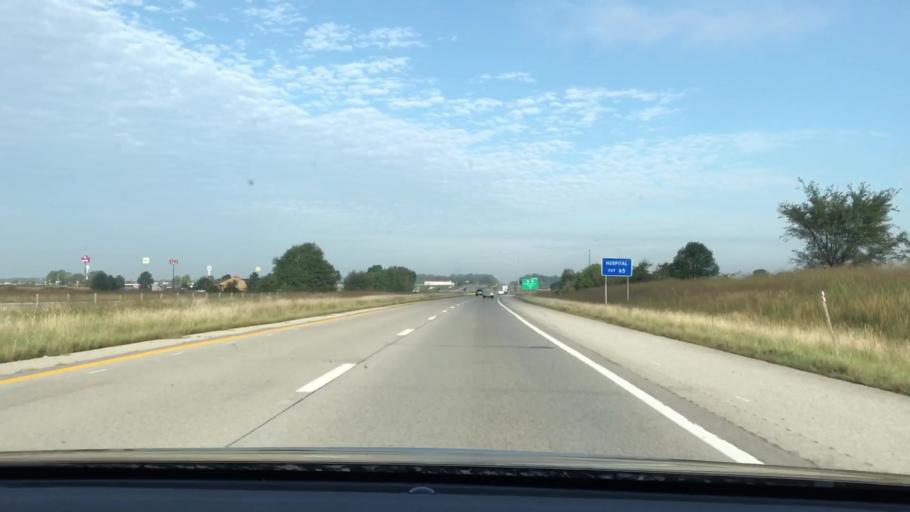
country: US
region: Kentucky
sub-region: Trigg County
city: Cadiz
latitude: 36.8774
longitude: -87.7276
